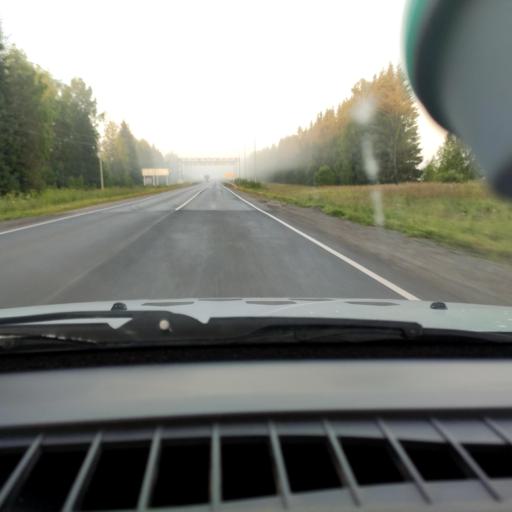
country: RU
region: Perm
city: Orda
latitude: 57.2604
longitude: 57.0107
